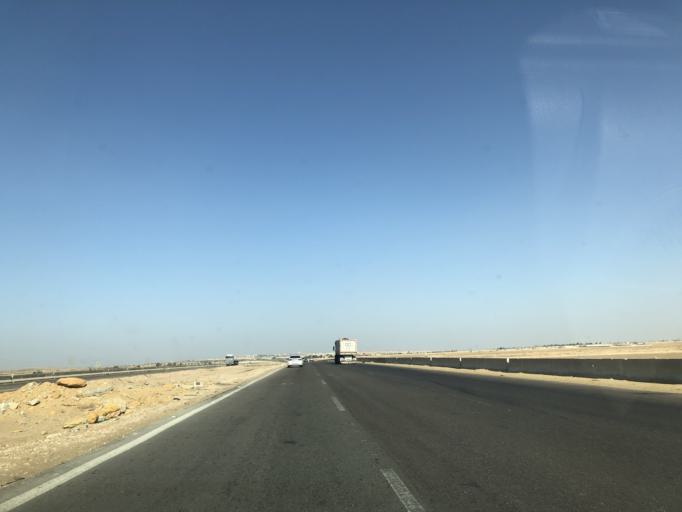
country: EG
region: Muhafazat al Minufiyah
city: Ashmun
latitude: 30.0678
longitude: 30.8895
